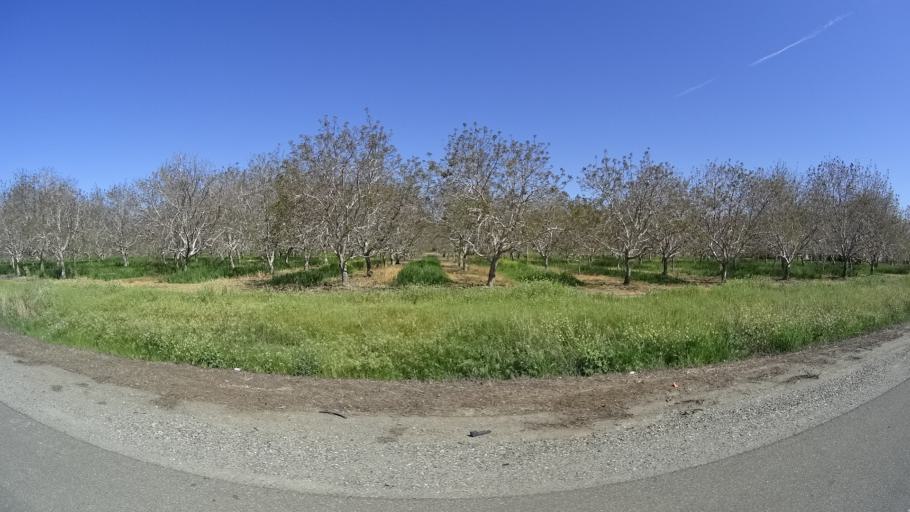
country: US
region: California
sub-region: Glenn County
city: Orland
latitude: 39.7468
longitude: -122.1198
